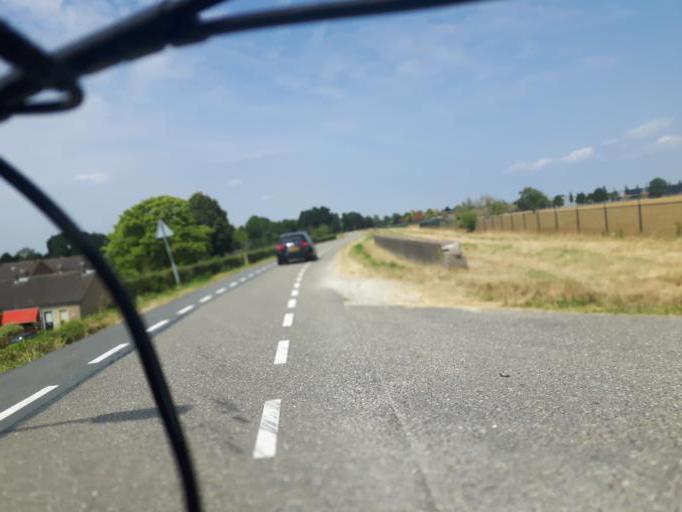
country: NL
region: Gelderland
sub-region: Gemeente Zaltbommel
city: Zaltbommel
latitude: 51.8148
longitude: 5.2160
